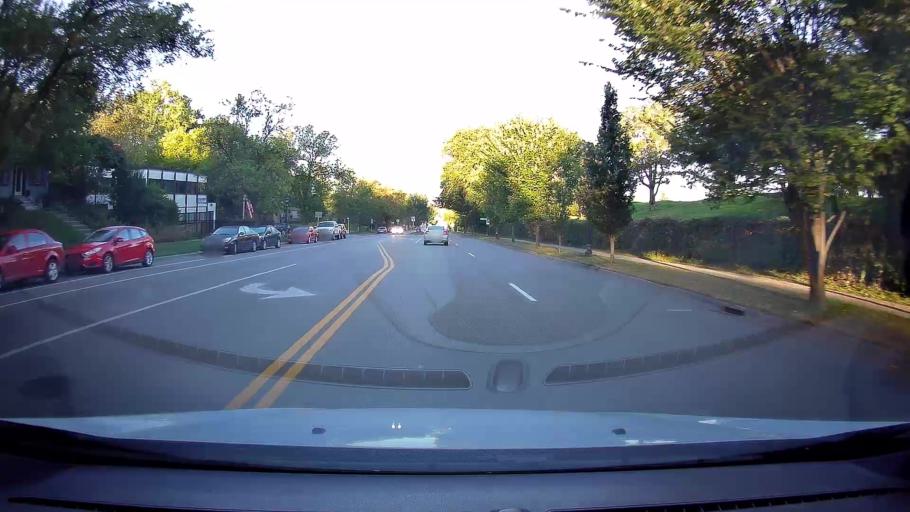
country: US
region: Minnesota
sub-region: Ramsey County
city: Falcon Heights
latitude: 44.9484
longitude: -93.1942
